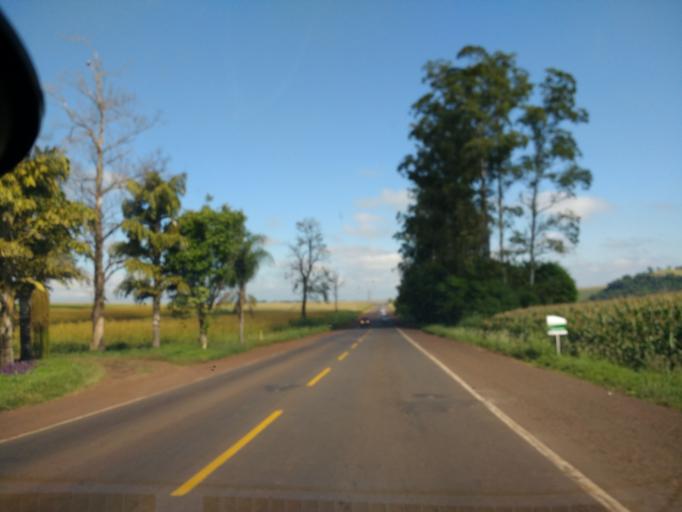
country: BR
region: Parana
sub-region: Paicandu
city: Paicandu
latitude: -23.5094
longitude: -52.1725
